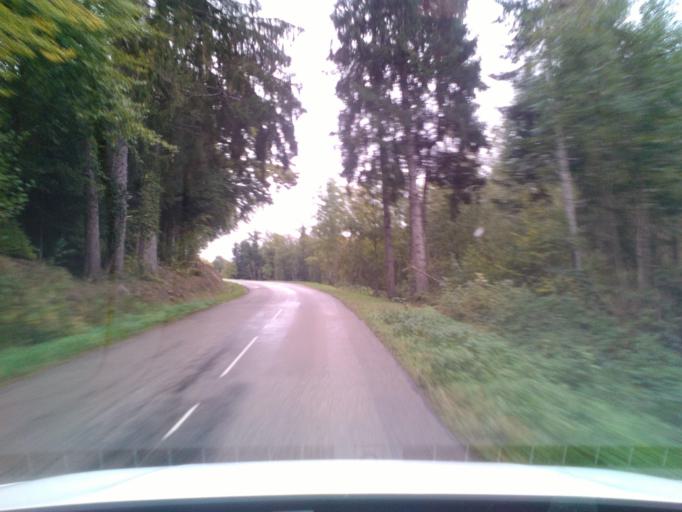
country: FR
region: Lorraine
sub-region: Departement des Vosges
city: Moyenmoutier
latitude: 48.3704
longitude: 6.9244
